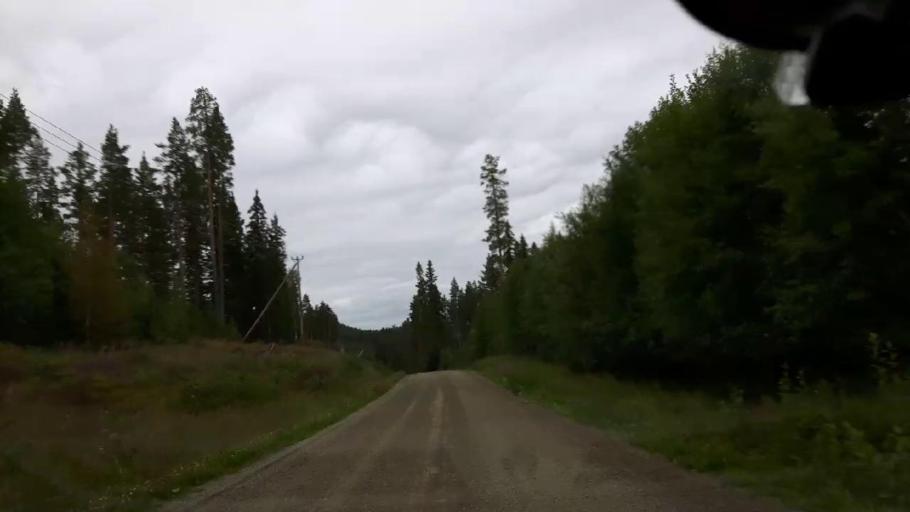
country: SE
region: Jaemtland
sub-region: Braecke Kommun
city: Braecke
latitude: 63.0092
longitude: 15.3806
